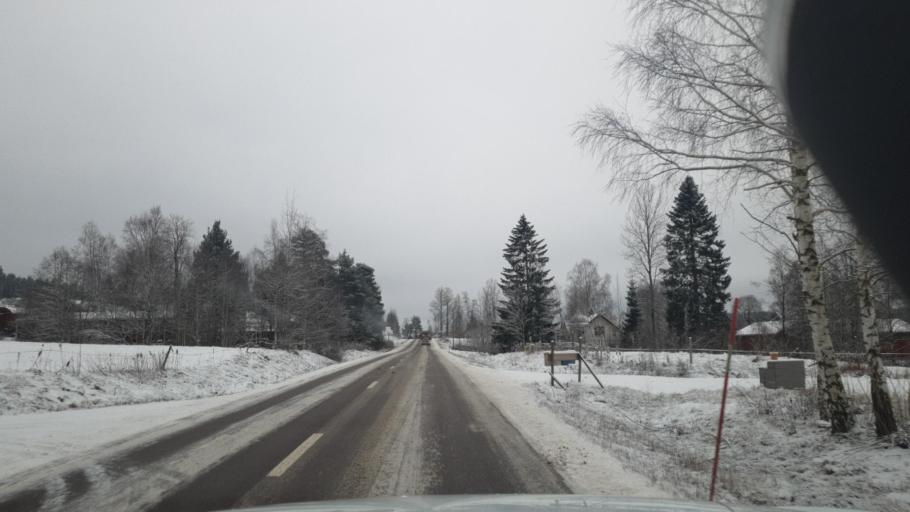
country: SE
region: Vaermland
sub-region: Eda Kommun
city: Amotfors
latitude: 59.6763
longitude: 12.1452
